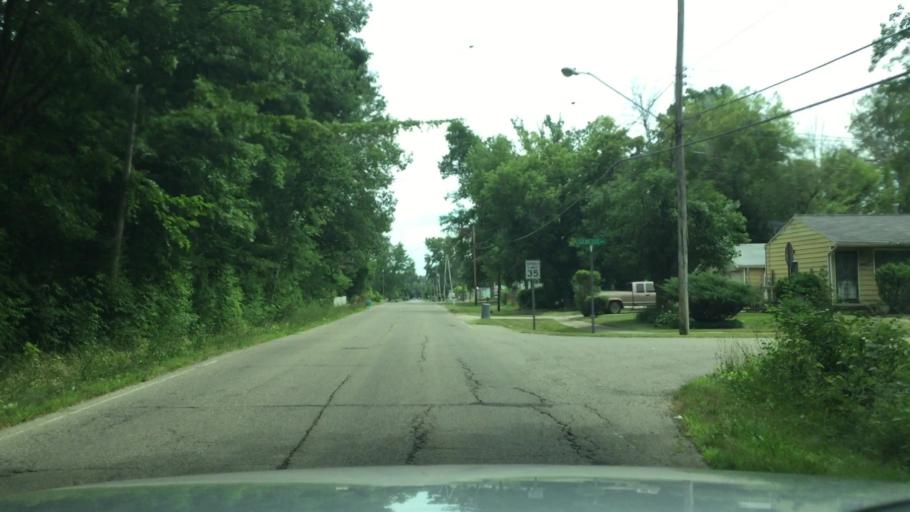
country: US
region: Michigan
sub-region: Genesee County
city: Beecher
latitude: 43.0828
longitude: -83.6817
